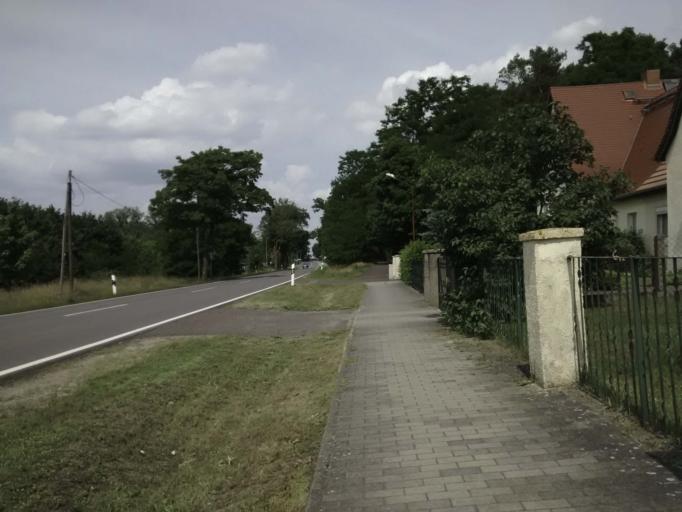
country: DE
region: Saxony-Anhalt
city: Hohenwarthe
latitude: 52.2459
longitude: 11.7390
